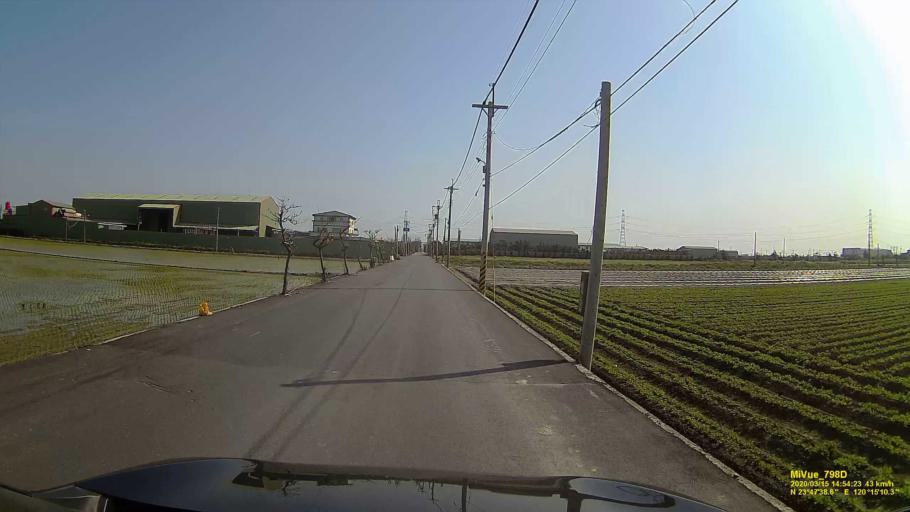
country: TW
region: Taiwan
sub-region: Yunlin
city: Douliu
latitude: 23.7939
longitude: 120.2529
